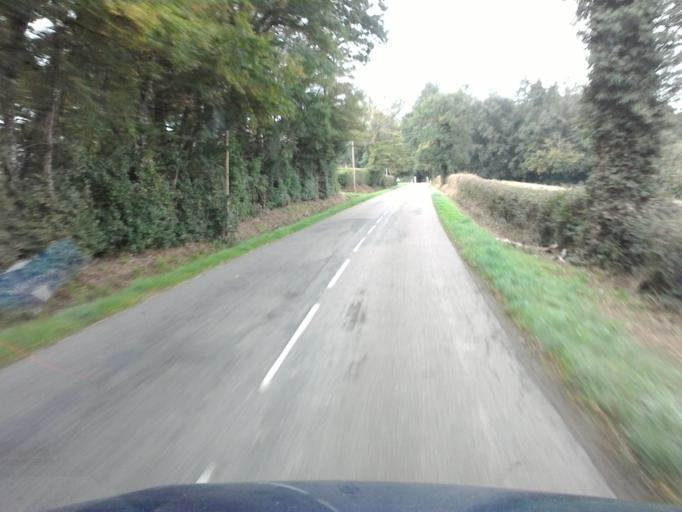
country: FR
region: Bourgogne
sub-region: Departement de la Nievre
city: Lormes
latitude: 47.2483
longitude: 3.8146
